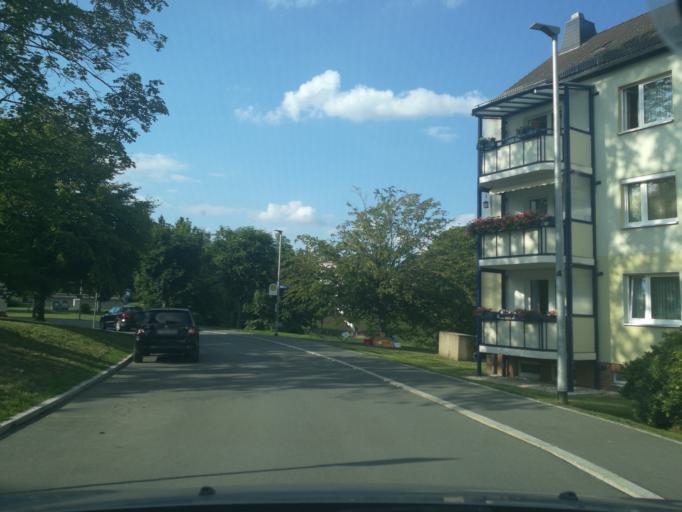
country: DE
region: Saxony
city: Adorf
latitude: 50.3150
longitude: 12.2522
